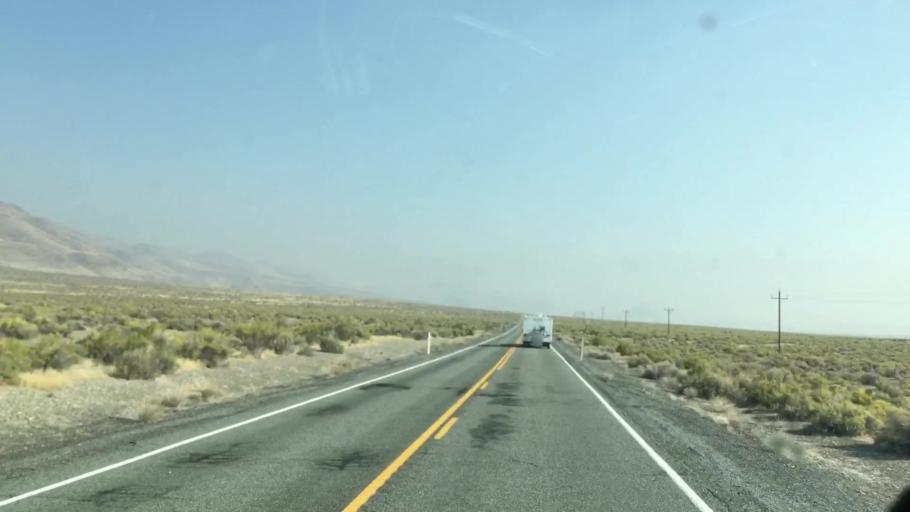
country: US
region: Nevada
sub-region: Lyon County
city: Fernley
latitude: 40.2345
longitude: -119.3679
